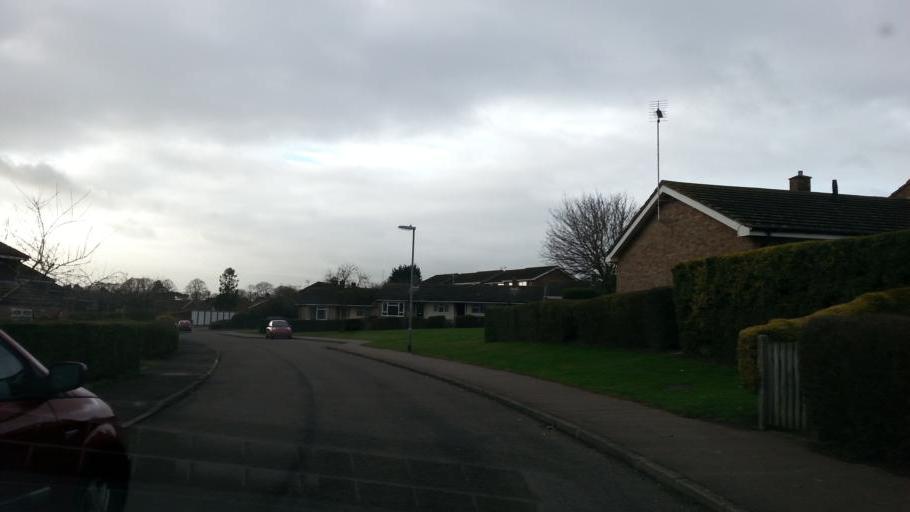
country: GB
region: England
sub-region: Cambridgeshire
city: Linton
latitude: 52.1014
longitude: 0.2869
